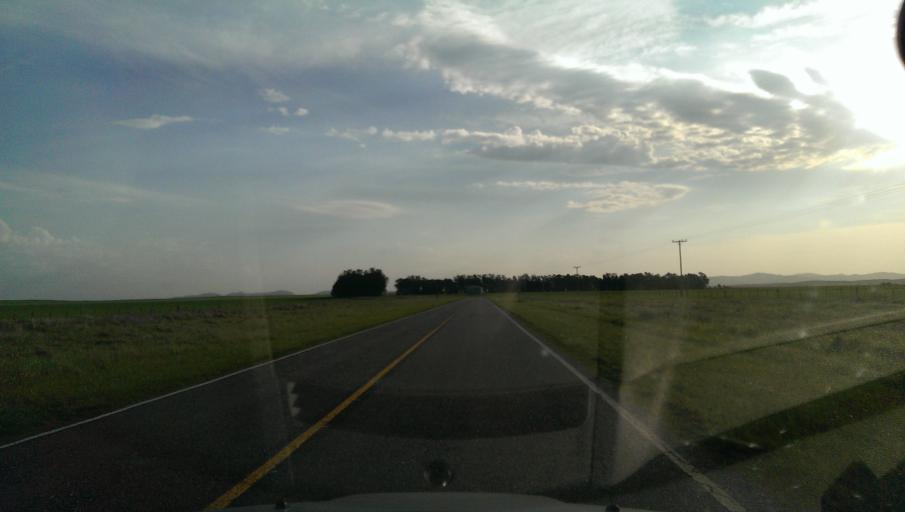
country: AR
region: Buenos Aires
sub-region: Partido de Coronel Suarez
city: Coronel Suarez
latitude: -37.8225
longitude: -61.8100
